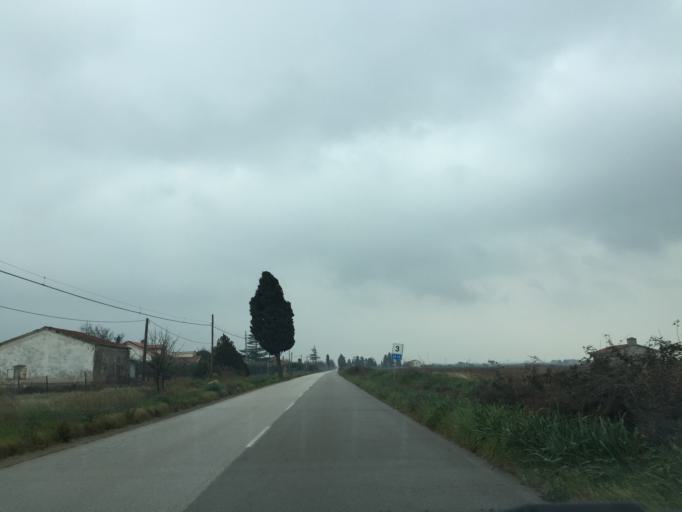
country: IT
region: Apulia
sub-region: Provincia di Foggia
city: Foggia
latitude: 41.4233
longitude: 15.4656
